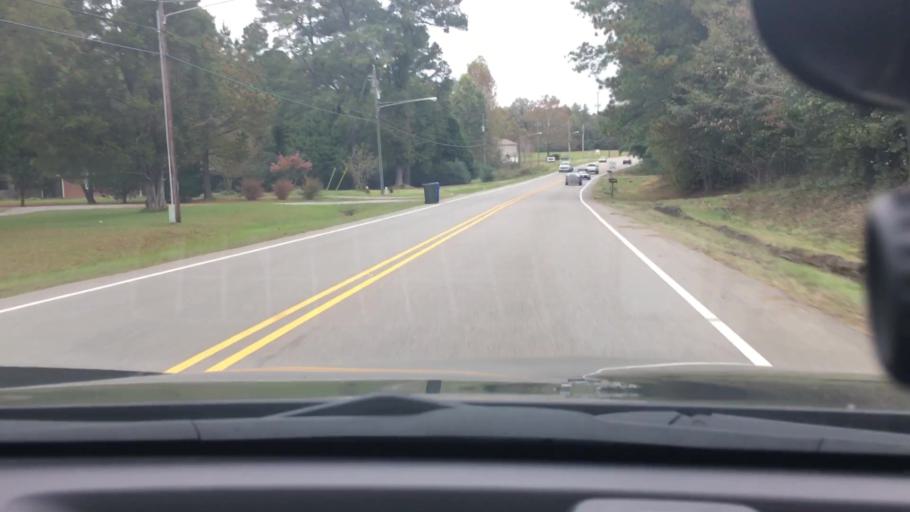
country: US
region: North Carolina
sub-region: Pitt County
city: Summerfield
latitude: 35.5887
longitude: -77.4091
